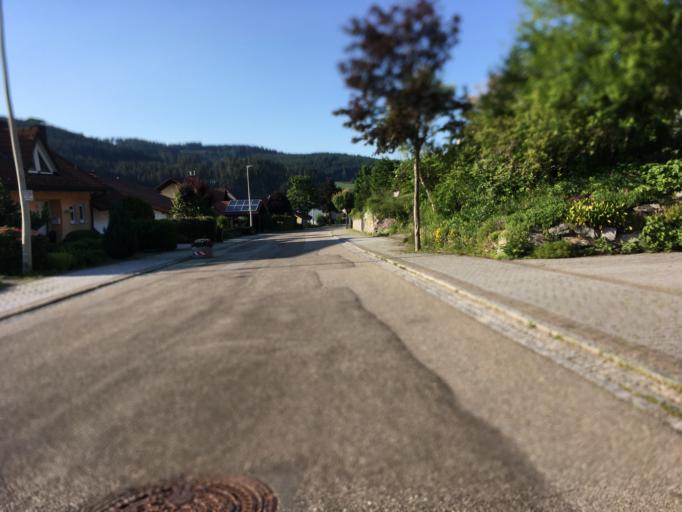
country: DE
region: Baden-Wuerttemberg
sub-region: Freiburg Region
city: Titisee-Neustadt
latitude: 47.9195
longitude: 8.2193
